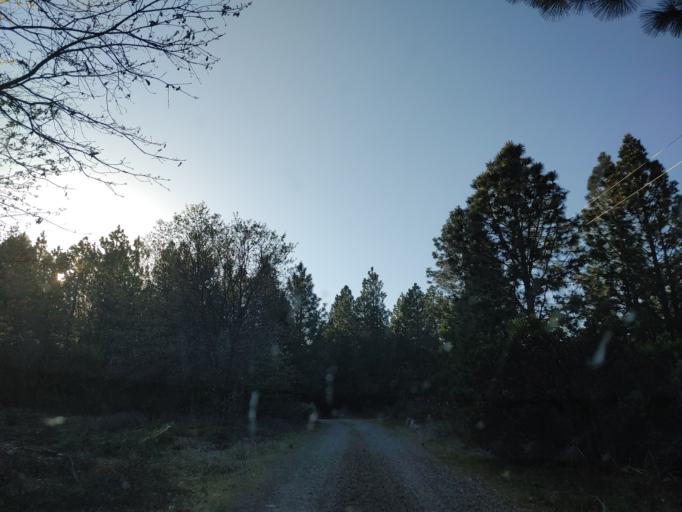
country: US
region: California
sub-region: Shasta County
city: Burney
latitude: 40.8115
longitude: -121.9456
